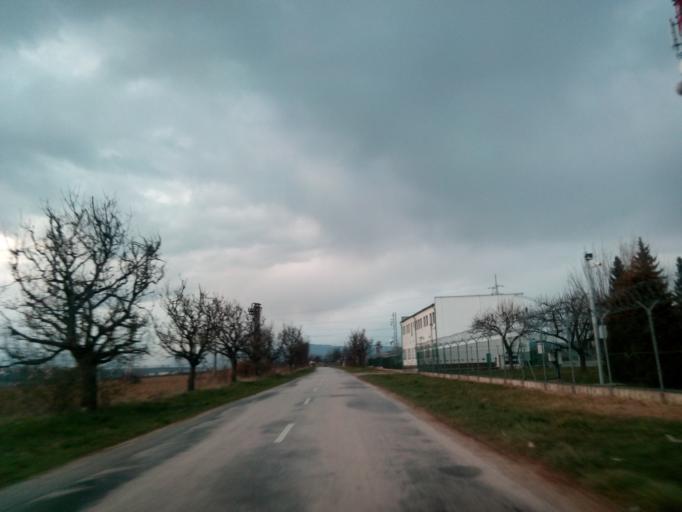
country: SK
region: Kosicky
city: Moldava nad Bodvou
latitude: 48.5926
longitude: 20.9957
